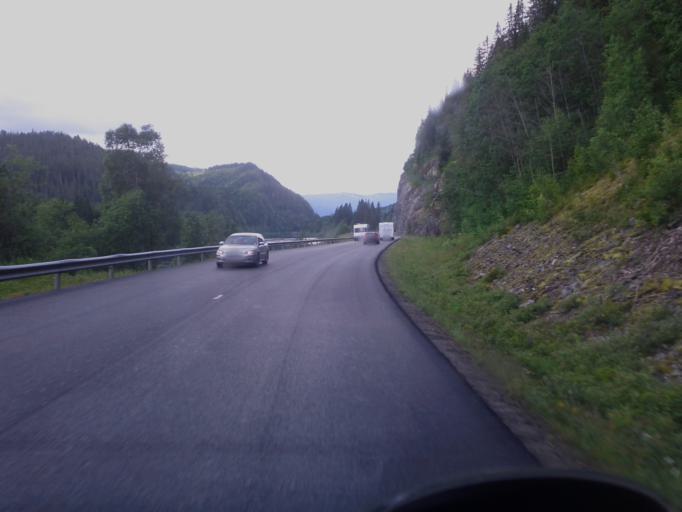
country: NO
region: Nord-Trondelag
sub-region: Grong
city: Grong
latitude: 64.5227
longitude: 12.3834
